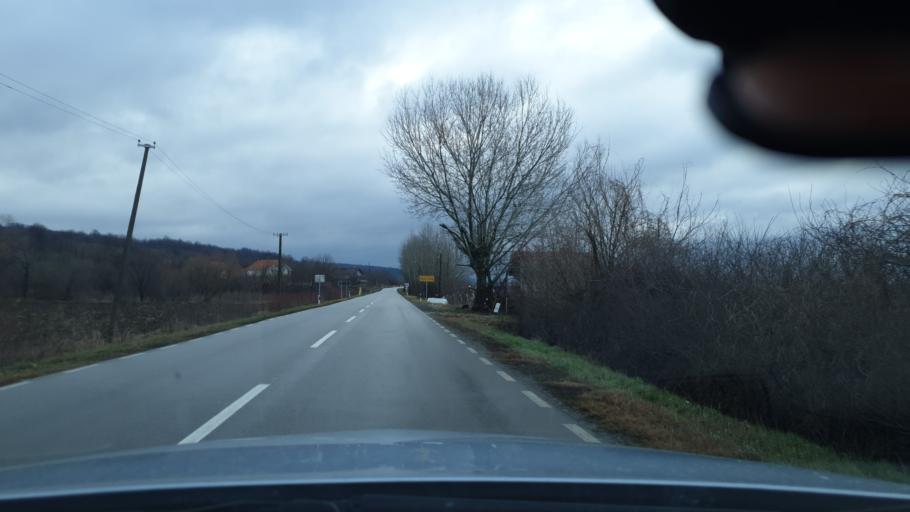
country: RS
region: Central Serbia
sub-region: Branicevski Okrug
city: Petrovac
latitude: 44.4301
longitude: 21.3596
